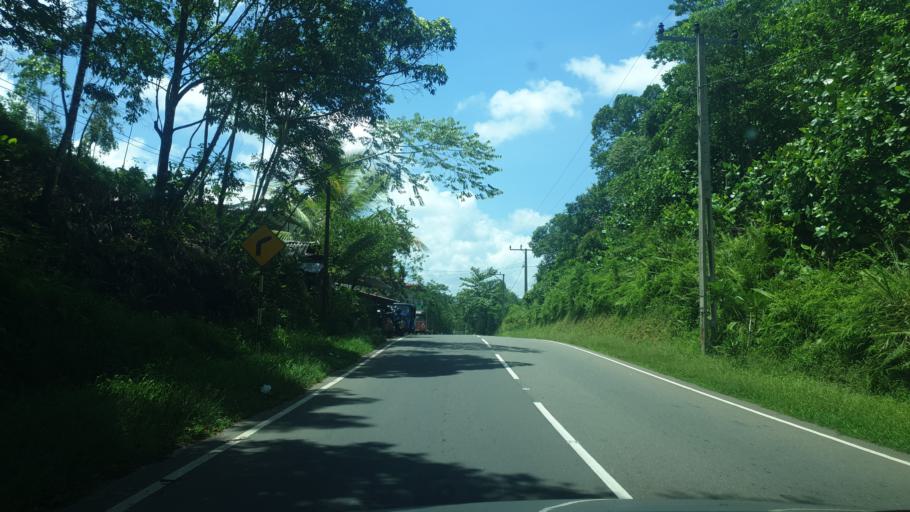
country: LK
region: Western
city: Horawala Junction
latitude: 6.5143
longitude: 80.2419
